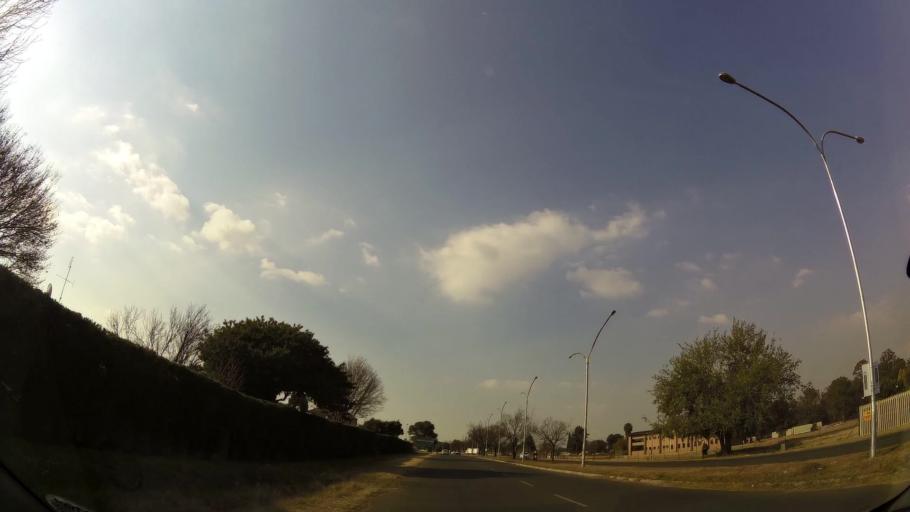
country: ZA
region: Gauteng
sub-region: Ekurhuleni Metropolitan Municipality
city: Benoni
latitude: -26.1375
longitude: 28.2904
